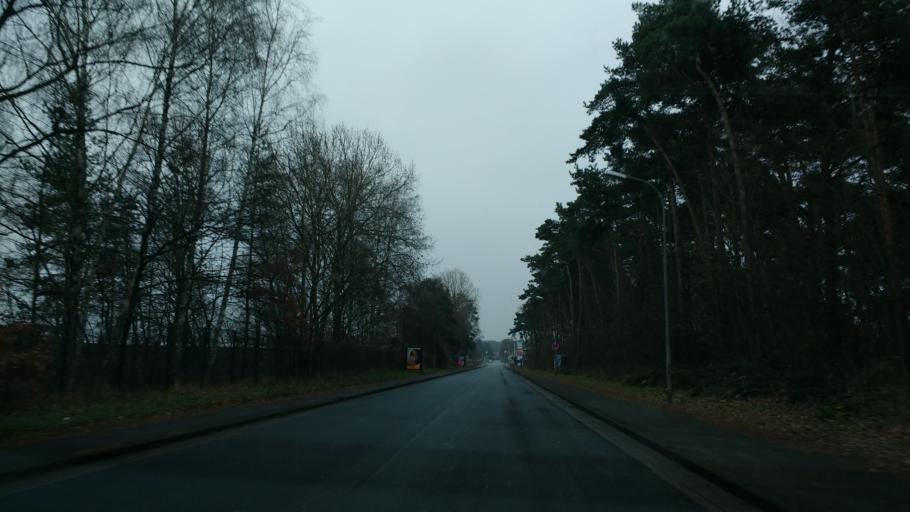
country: DE
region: Lower Saxony
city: Garbsen
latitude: 52.4197
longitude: 9.5692
